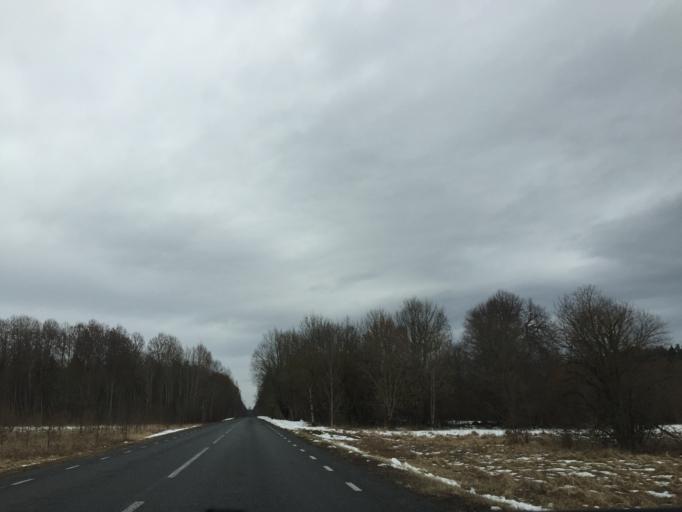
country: EE
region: Saare
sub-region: Orissaare vald
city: Orissaare
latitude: 58.5684
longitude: 22.7622
